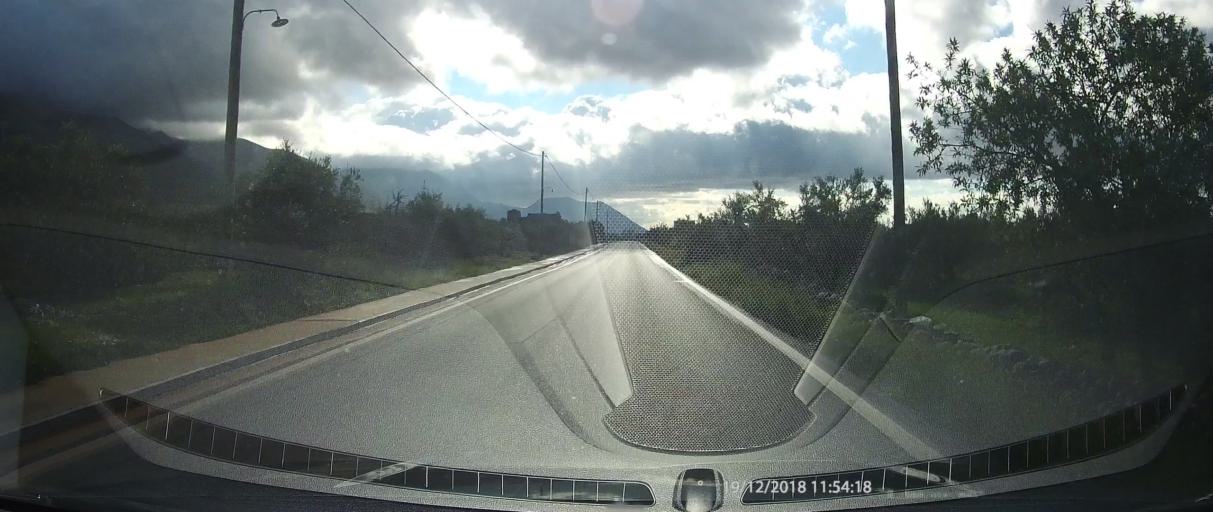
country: GR
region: Peloponnese
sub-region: Nomos Lakonias
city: Gytheio
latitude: 36.6201
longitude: 22.3903
